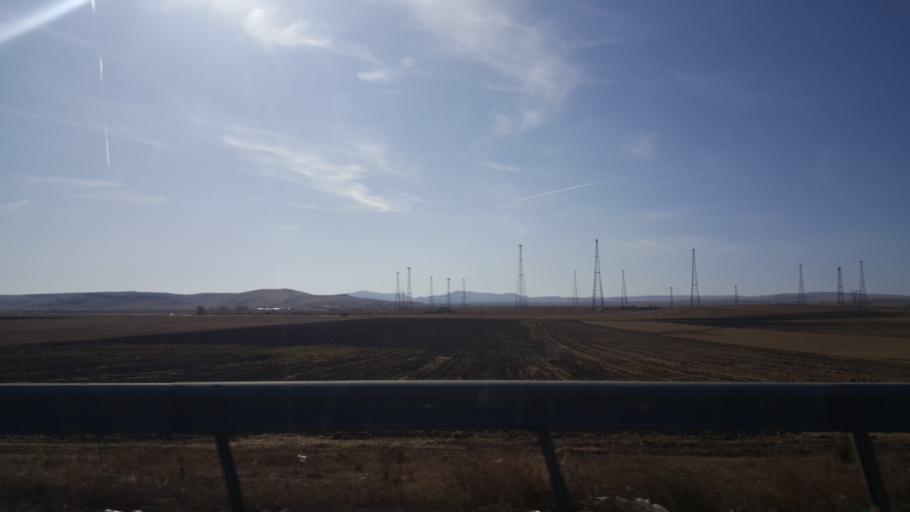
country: TR
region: Ankara
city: Yenice
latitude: 39.4049
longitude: 32.8726
